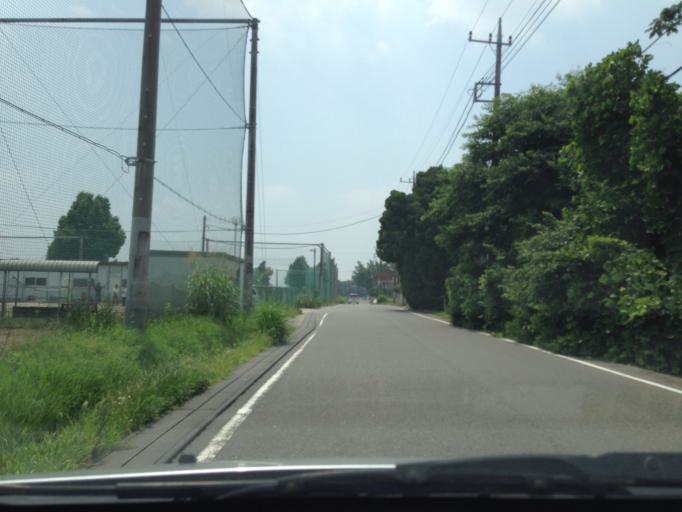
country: JP
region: Ibaraki
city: Naka
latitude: 36.0459
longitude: 140.1264
